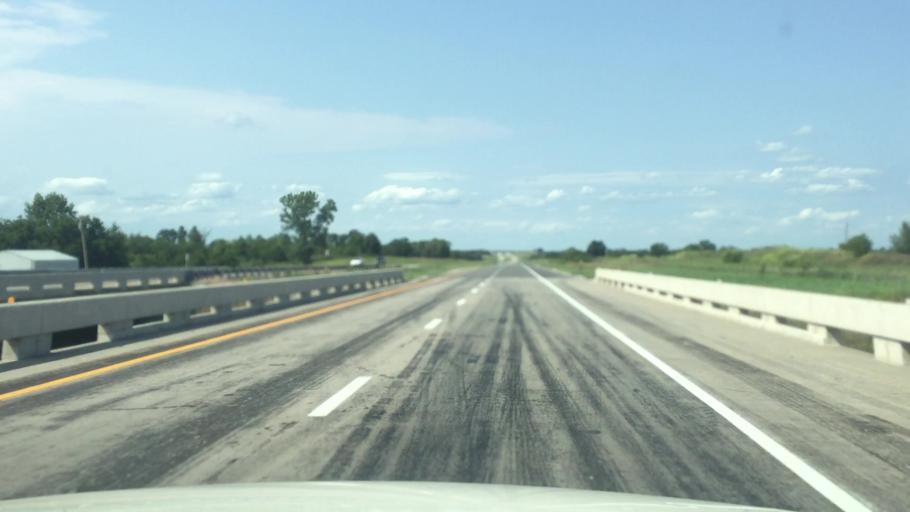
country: US
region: Kansas
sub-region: Linn County
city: La Cygne
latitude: 38.3742
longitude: -94.6874
